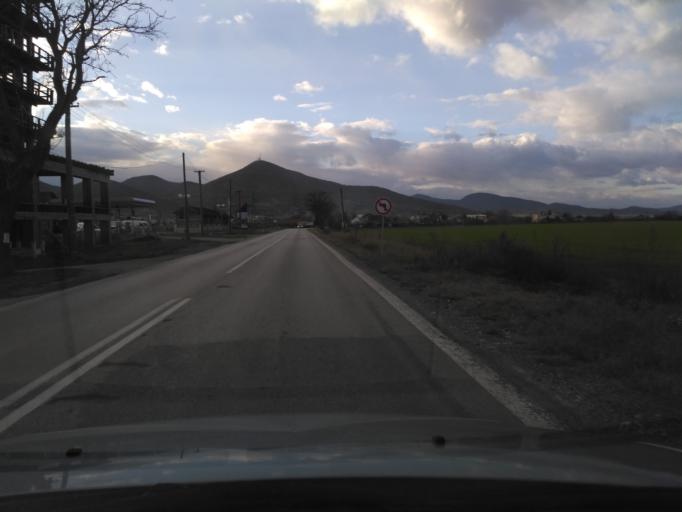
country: HU
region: Borsod-Abauj-Zemplen
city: Satoraljaujhely
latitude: 48.3978
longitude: 21.6841
